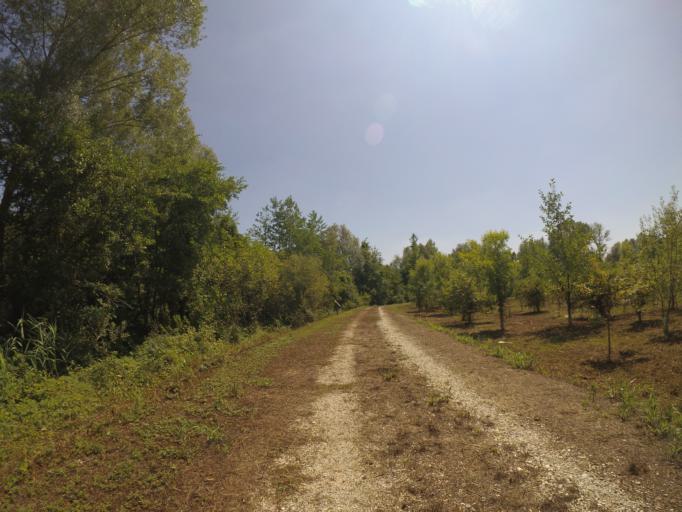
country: IT
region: Friuli Venezia Giulia
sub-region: Provincia di Udine
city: Rivignano
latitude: 45.8981
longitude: 13.0723
